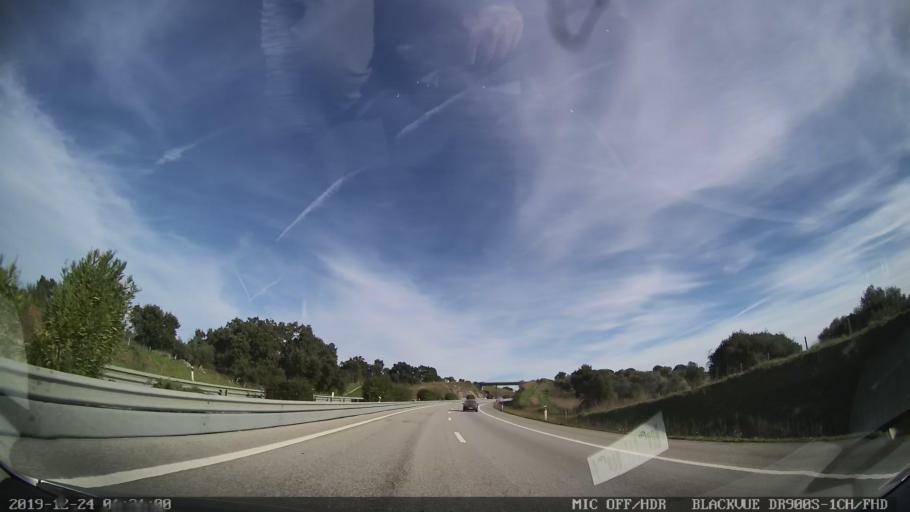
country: PT
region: Santarem
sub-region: Abrantes
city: Alferrarede
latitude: 39.4922
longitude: -8.1135
